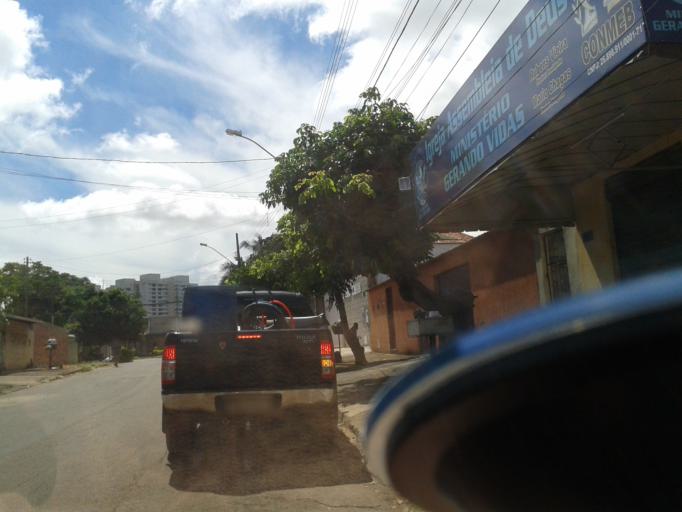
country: BR
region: Goias
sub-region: Goiania
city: Goiania
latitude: -16.6514
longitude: -49.3415
